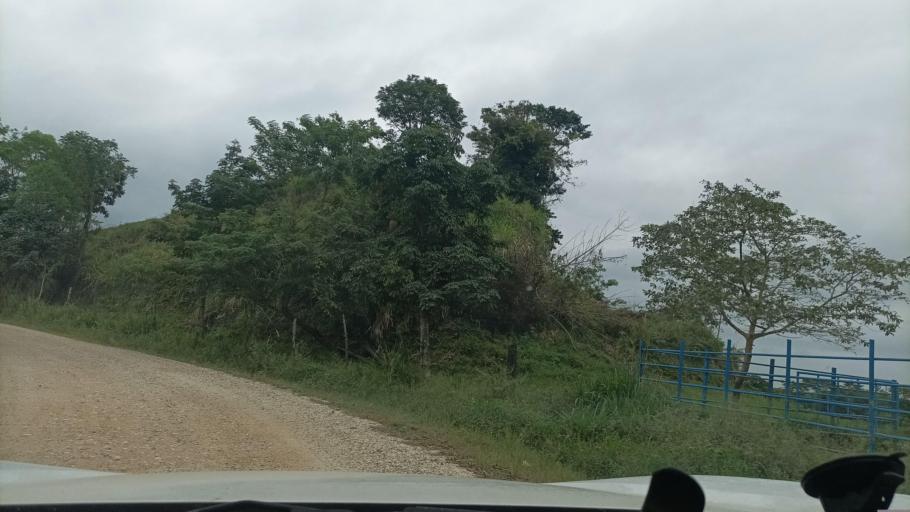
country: MX
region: Veracruz
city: Hidalgotitlan
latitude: 17.6224
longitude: -94.5135
